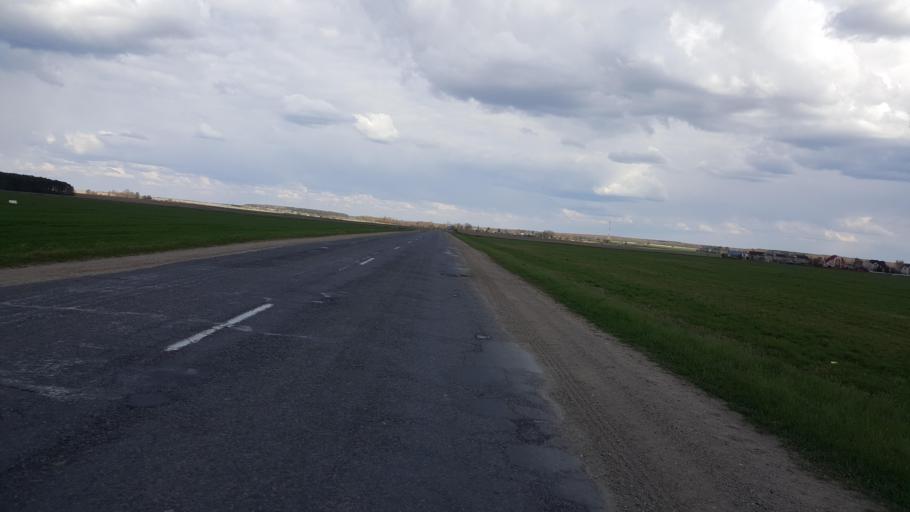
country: BY
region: Brest
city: Kamyanyets
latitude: 52.4154
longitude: 23.6312
